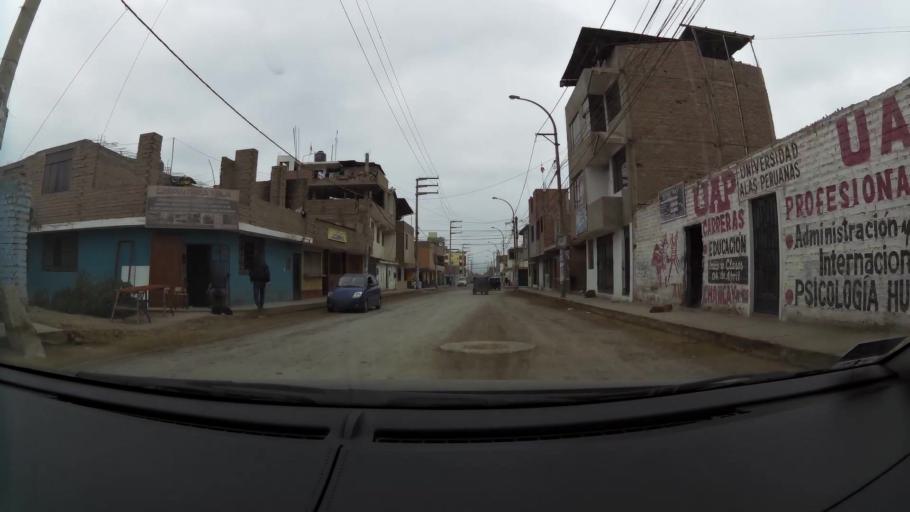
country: PE
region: Lima
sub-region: Provincia de Huaral
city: Huaral
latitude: -11.4891
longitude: -77.2040
